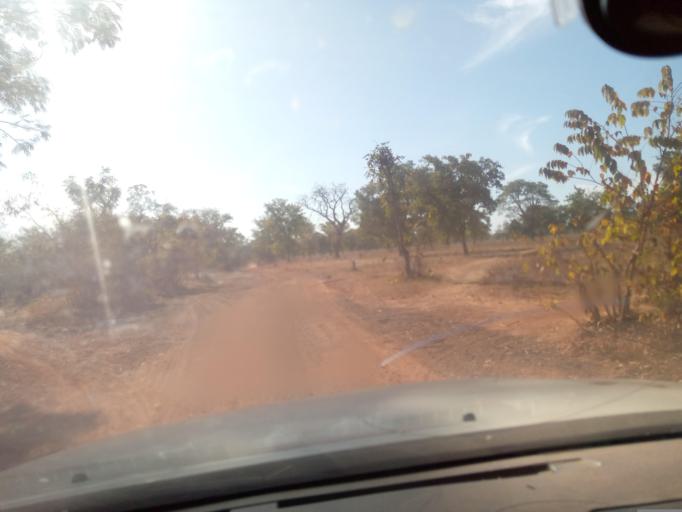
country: ML
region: Sikasso
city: Sikasso
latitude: 11.4593
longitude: -5.3287
